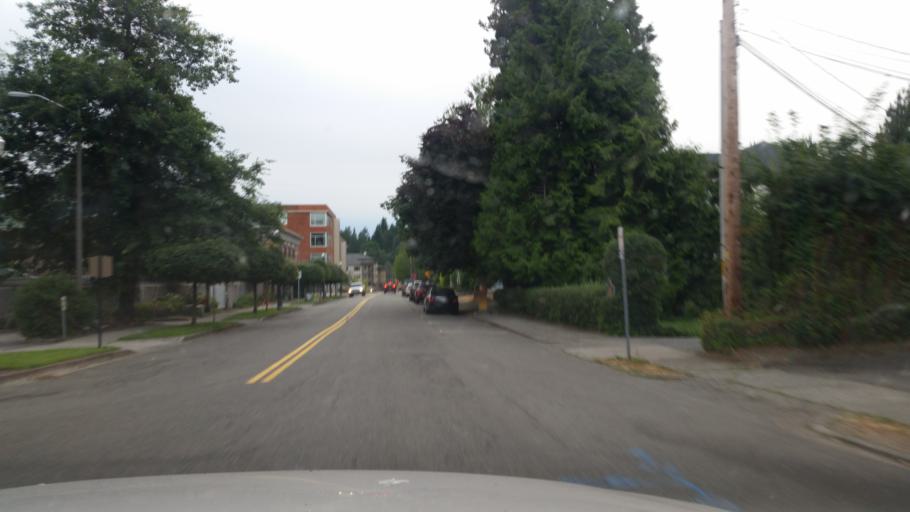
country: US
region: Washington
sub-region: King County
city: Bothell
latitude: 47.7619
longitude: -122.2040
